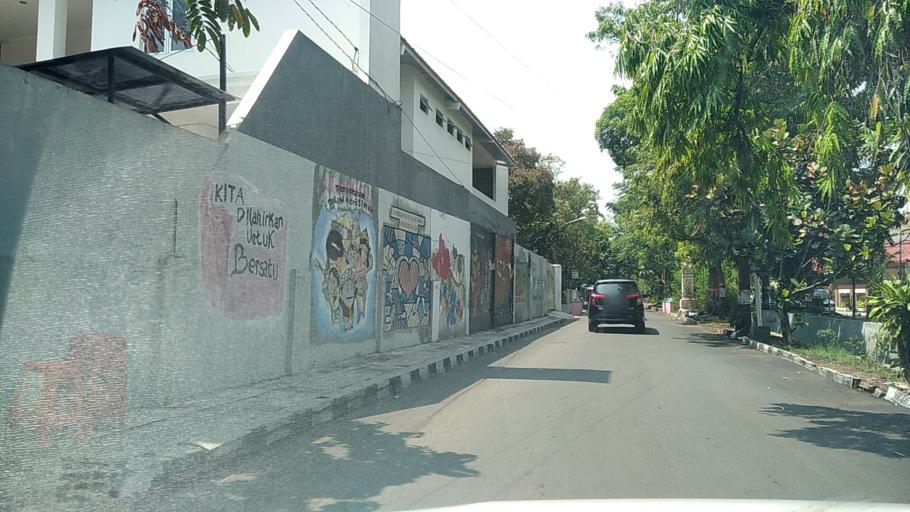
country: ID
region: Central Java
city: Semarang
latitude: -7.0066
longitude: 110.4394
